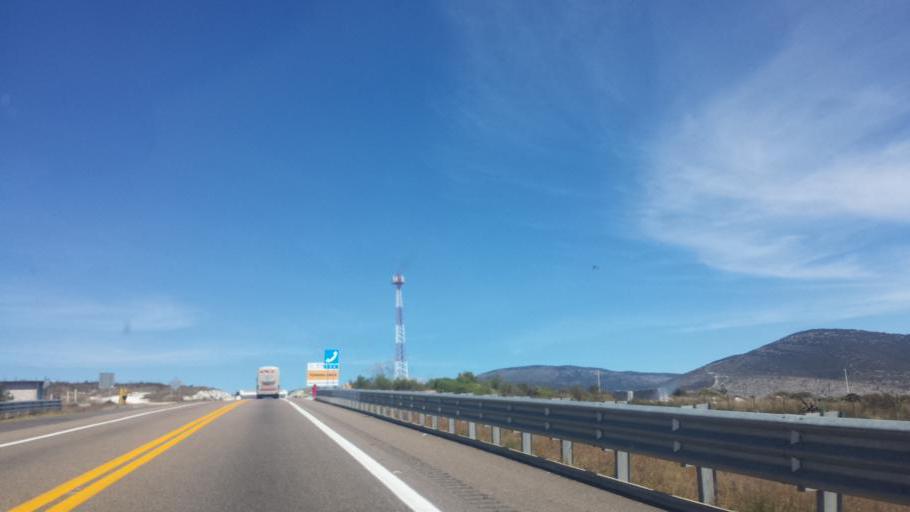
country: MX
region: Oaxaca
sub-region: Villa Tejupam de la Union
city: Villa Tejupam de la Union
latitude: 17.8892
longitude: -97.3717
